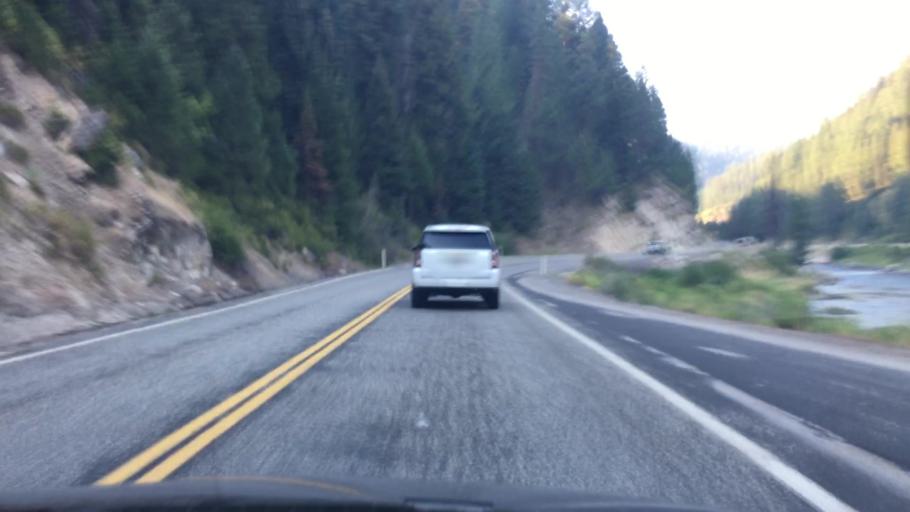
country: US
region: Idaho
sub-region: Valley County
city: Cascade
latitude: 44.3205
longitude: -116.0613
